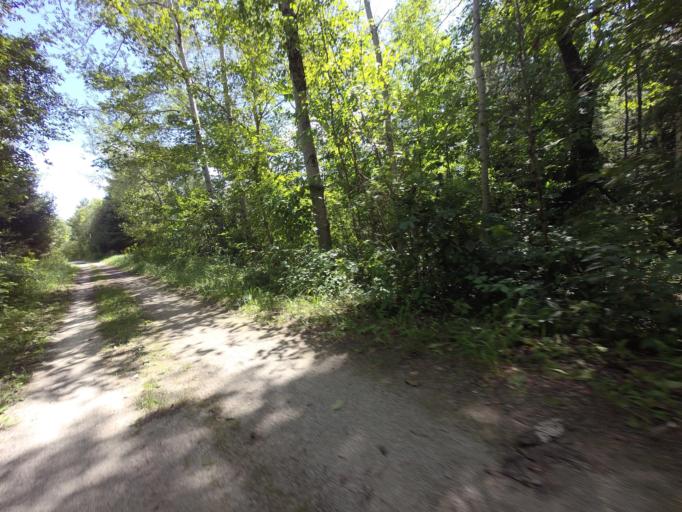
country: CA
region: Ontario
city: Orangeville
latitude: 43.7790
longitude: -80.1245
